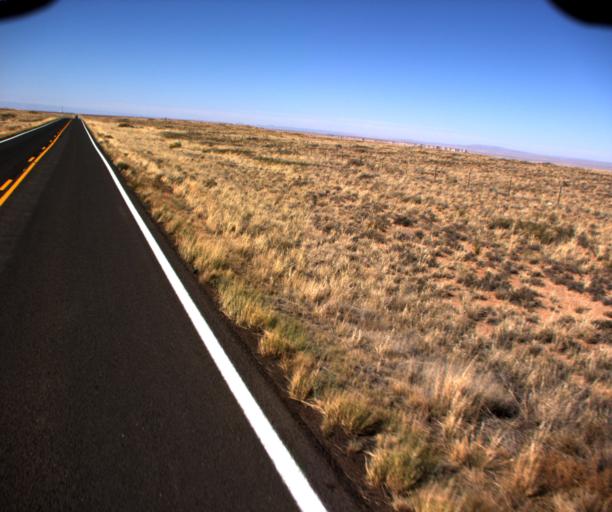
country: US
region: Arizona
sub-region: Coconino County
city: Tuba City
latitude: 35.9714
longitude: -110.9650
